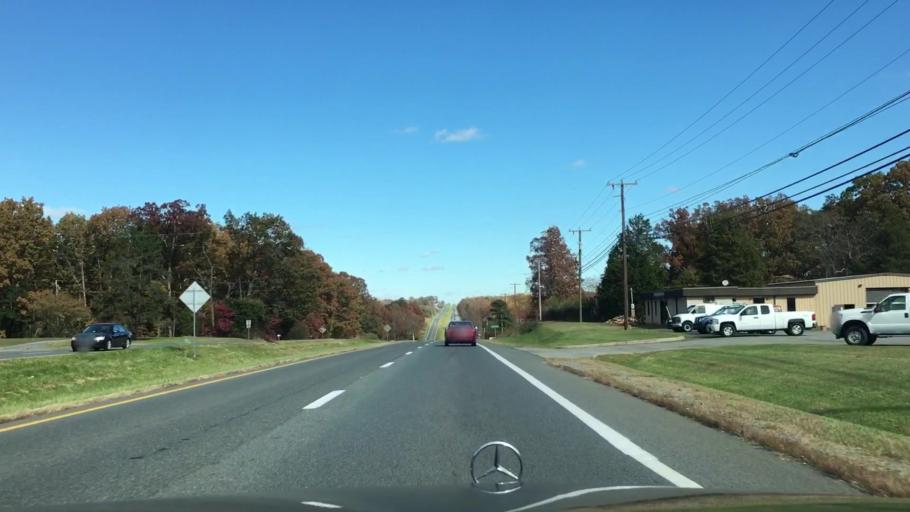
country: US
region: Virginia
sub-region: Campbell County
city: Rustburg
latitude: 37.2568
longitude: -79.1841
